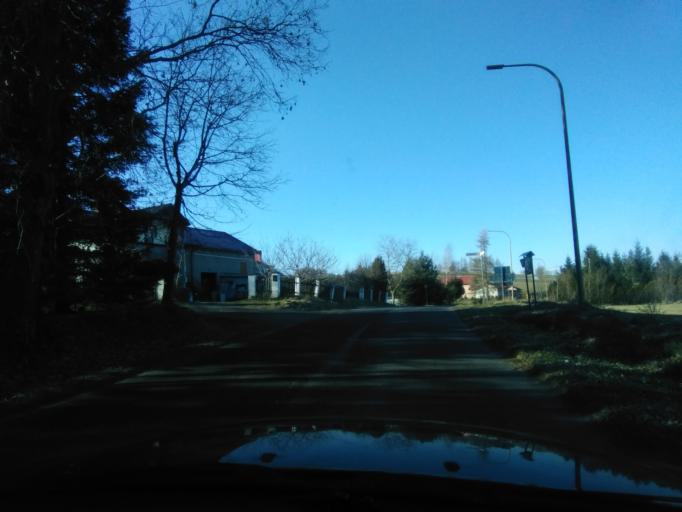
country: PL
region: Subcarpathian Voivodeship
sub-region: Powiat krosnienski
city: Rymanow
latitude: 49.5644
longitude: 21.8919
